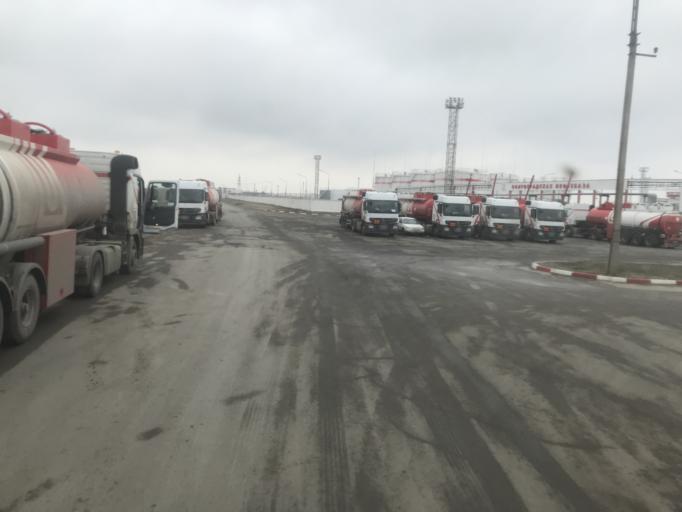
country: RU
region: Volgograd
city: Svetlyy Yar
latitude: 48.5098
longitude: 44.6398
